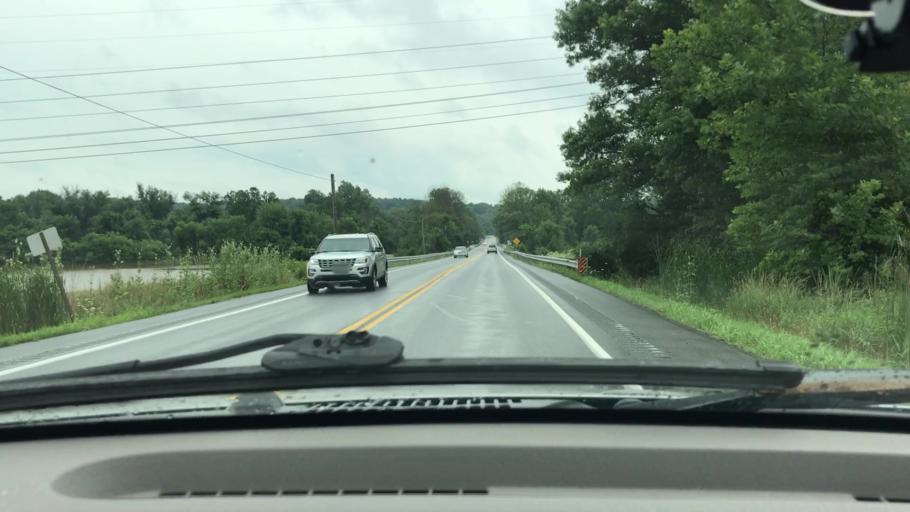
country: US
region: Pennsylvania
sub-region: Lancaster County
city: Elizabethtown
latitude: 40.1922
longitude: -76.6057
